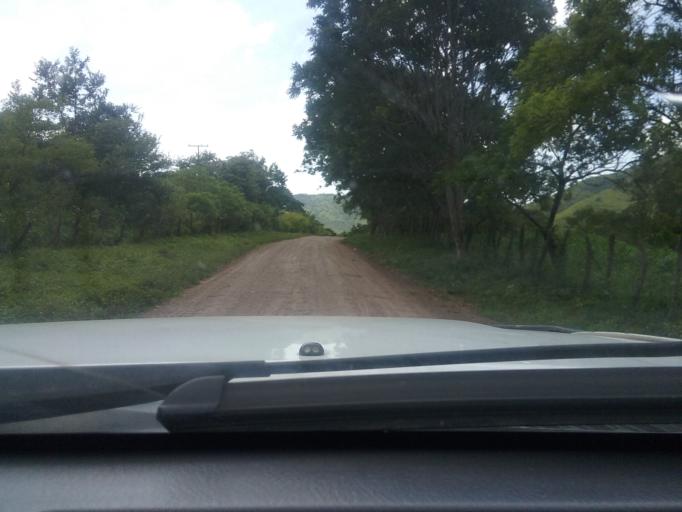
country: NI
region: Matagalpa
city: Terrabona
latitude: 12.7104
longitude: -85.9588
